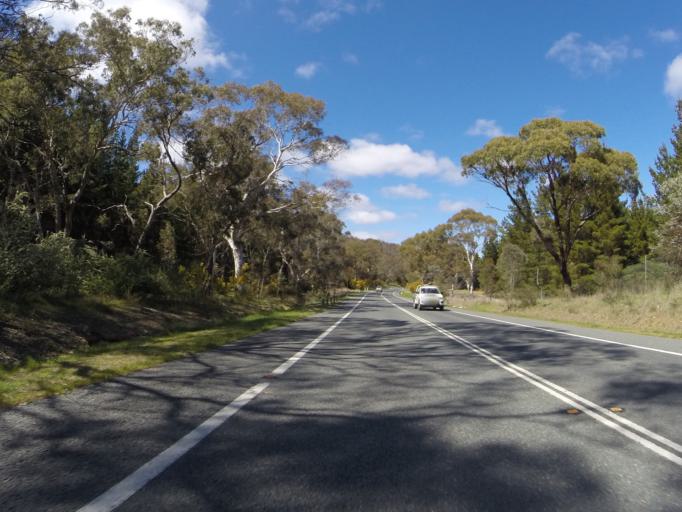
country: AU
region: New South Wales
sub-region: Queanbeyan
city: Queanbeyan
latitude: -35.2793
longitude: 149.2593
